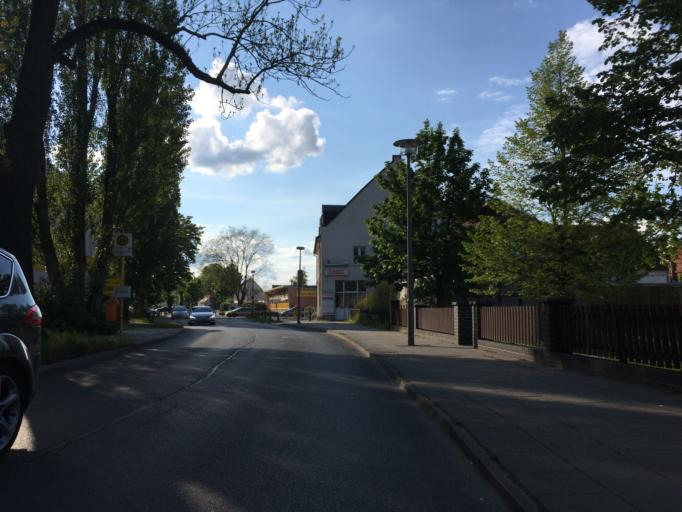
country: DE
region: Berlin
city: Wartenberg
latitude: 52.5746
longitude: 13.5192
